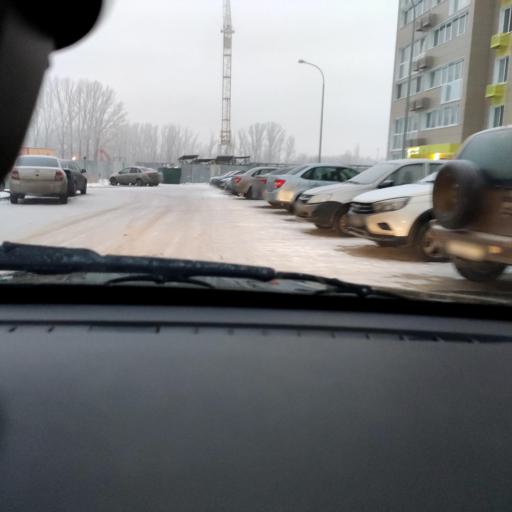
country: RU
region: Samara
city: Tol'yatti
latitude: 53.5473
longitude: 49.3112
